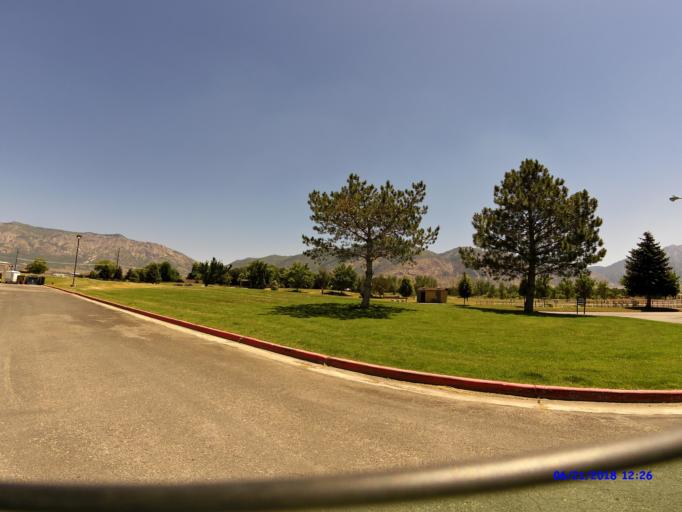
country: US
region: Utah
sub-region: Weber County
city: Harrisville
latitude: 41.2818
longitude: -111.9977
